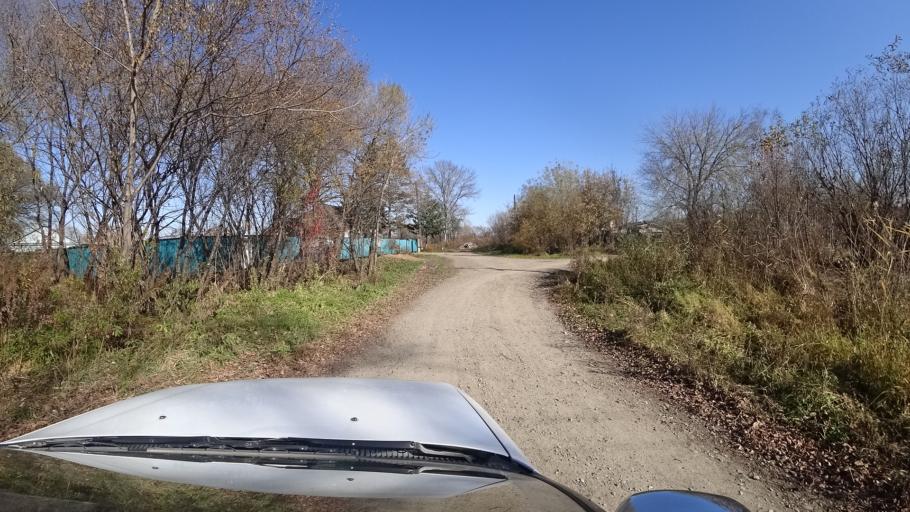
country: RU
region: Primorskiy
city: Dal'nerechensk
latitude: 45.9143
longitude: 133.8013
